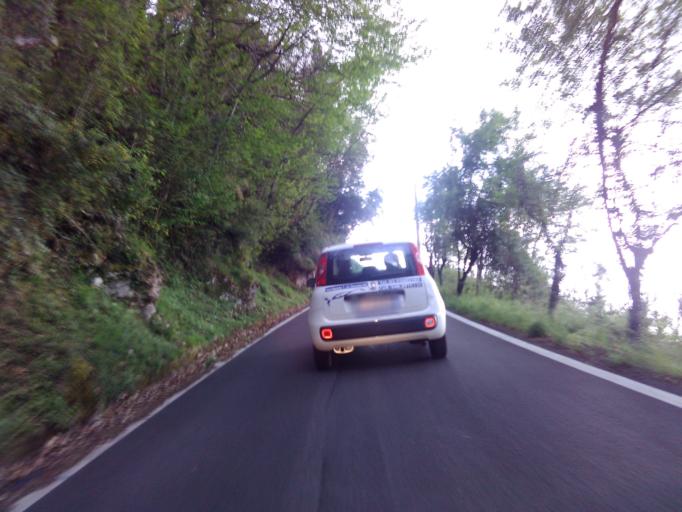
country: IT
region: Tuscany
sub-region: Provincia di Lucca
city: Pontestazzemese
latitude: 43.9612
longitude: 10.2783
